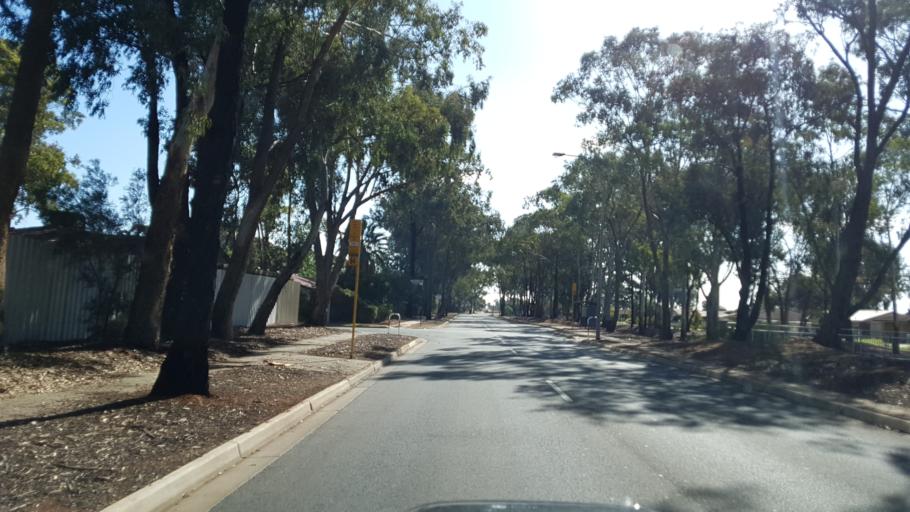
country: AU
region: South Australia
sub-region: Salisbury
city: Salisbury
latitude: -34.7367
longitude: 138.6208
